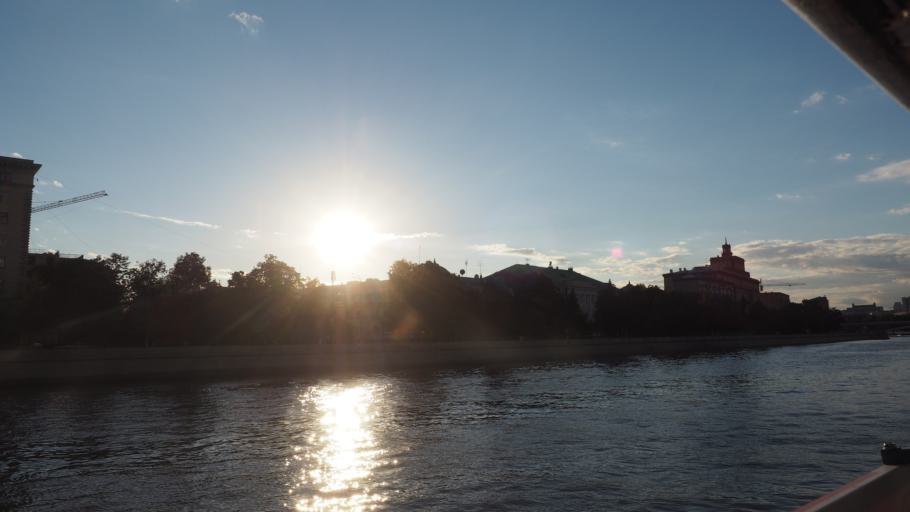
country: RU
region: Moscow
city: Zamoskvorech'ye
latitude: 55.7412
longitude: 37.6453
